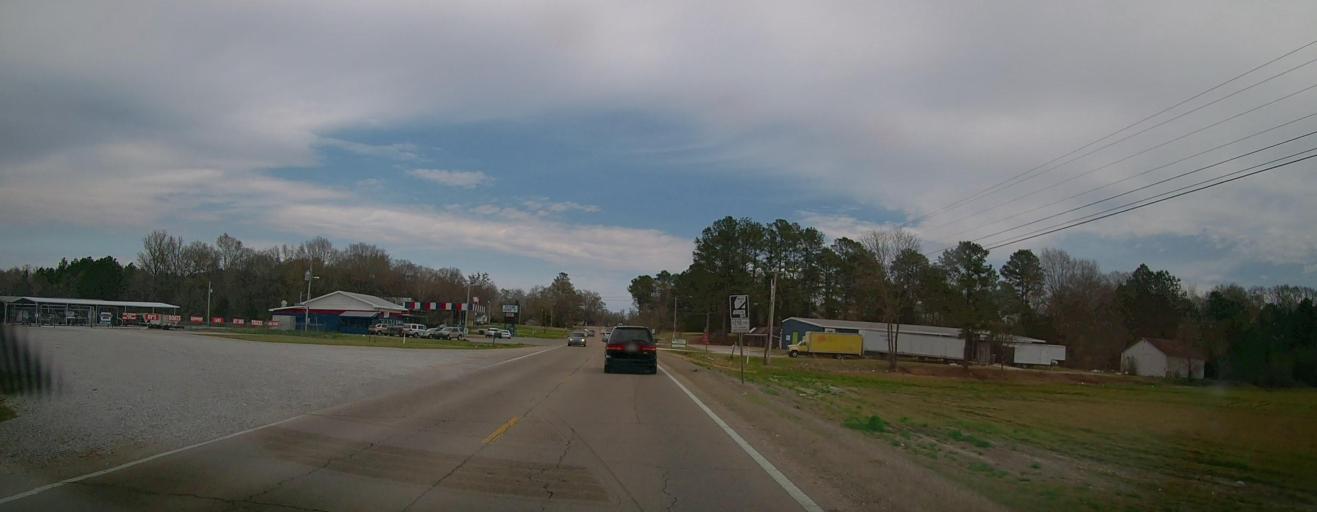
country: US
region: Mississippi
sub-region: Lee County
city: Plantersville
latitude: 34.2605
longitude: -88.6475
